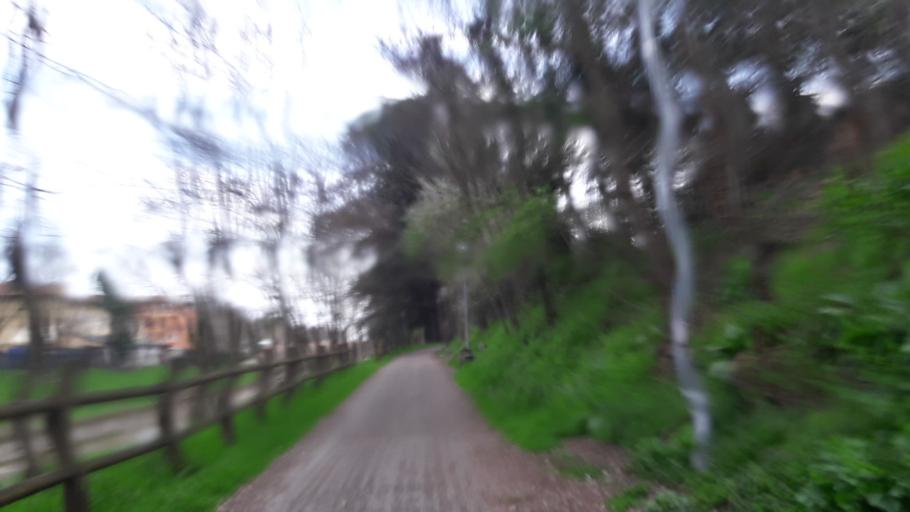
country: IT
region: Emilia-Romagna
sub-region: Provincia di Reggio Emilia
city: Reggio nell'Emilia
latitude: 44.6859
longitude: 10.6220
